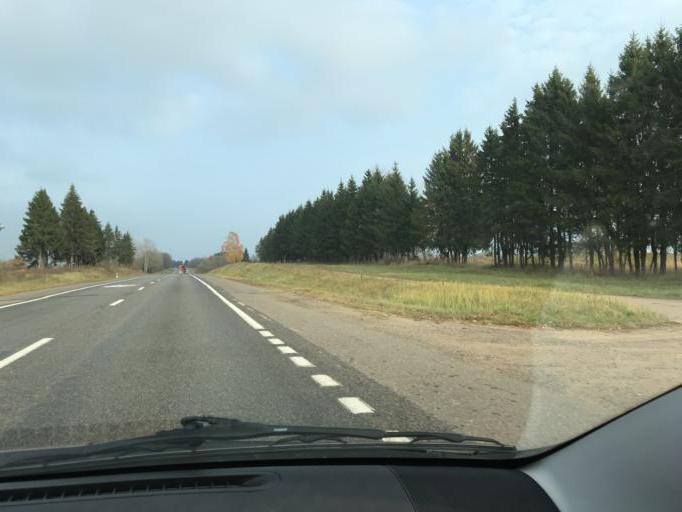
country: BY
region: Vitebsk
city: Syanno
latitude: 55.1348
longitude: 29.8114
